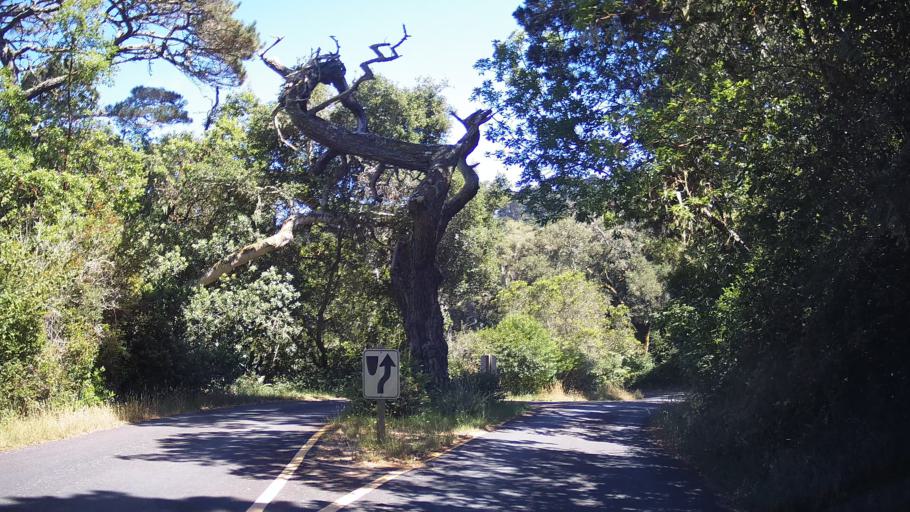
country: US
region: California
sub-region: Marin County
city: Inverness
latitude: 38.1332
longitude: -122.8955
